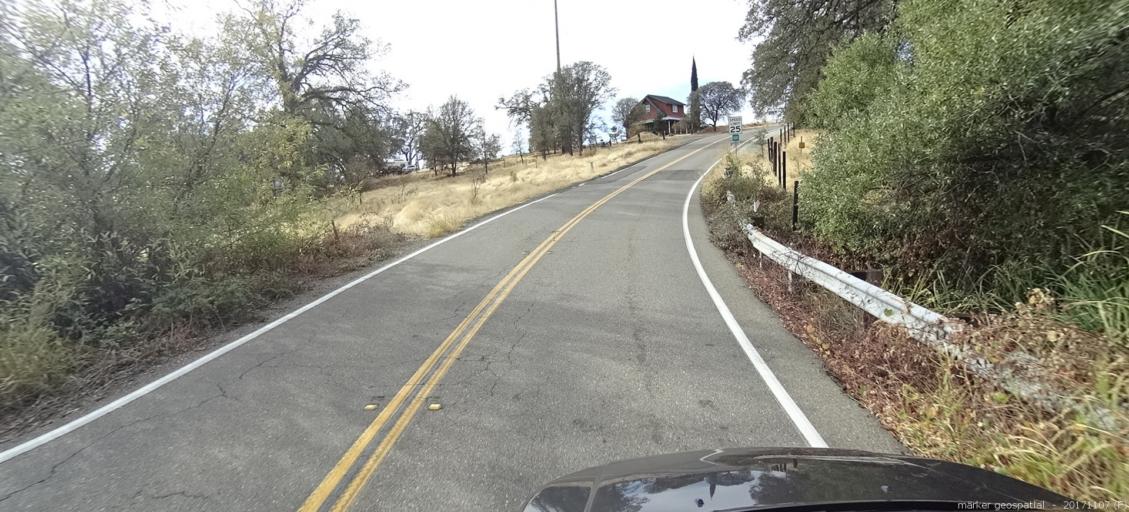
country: US
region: California
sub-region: Shasta County
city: Shasta
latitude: 40.5066
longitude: -122.5388
